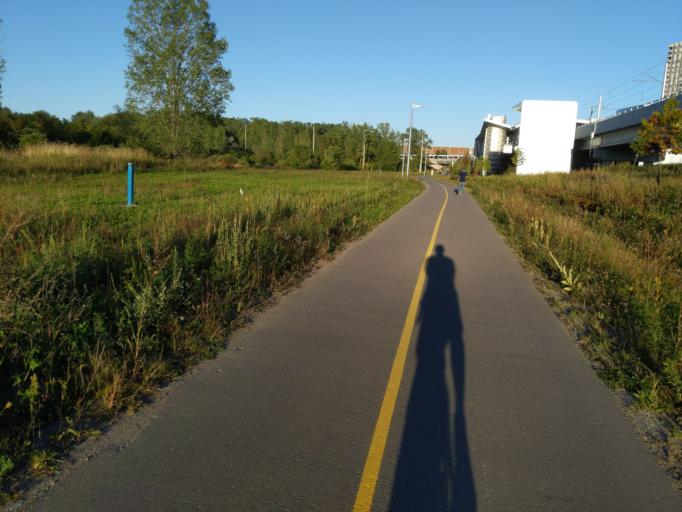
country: CA
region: Ontario
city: Ottawa
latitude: 45.4124
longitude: -75.6662
